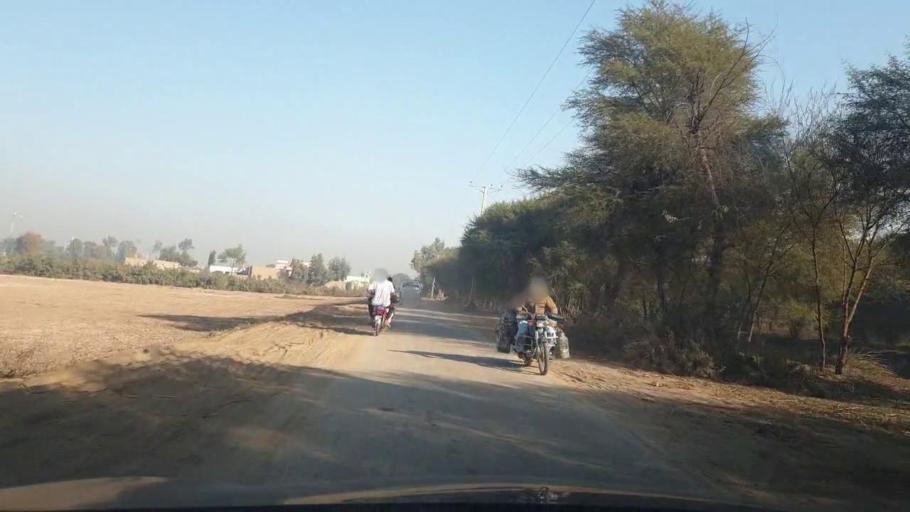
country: PK
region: Sindh
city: Mirpur Mathelo
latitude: 28.0710
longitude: 69.4670
